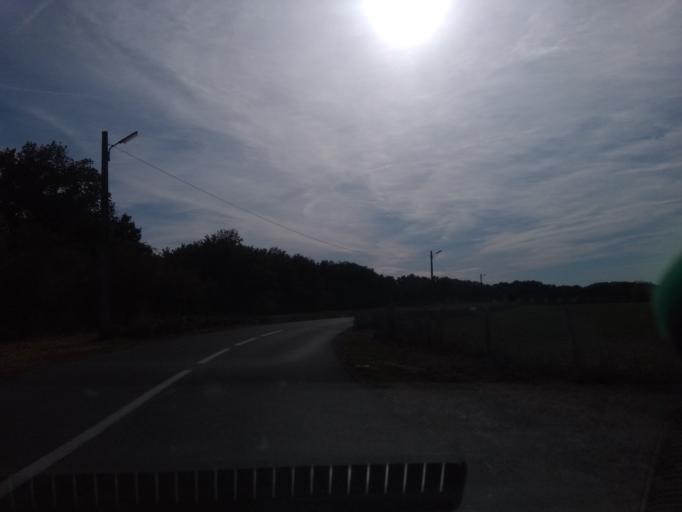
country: FR
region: Poitou-Charentes
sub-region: Departement de la Vienne
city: Saulge
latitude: 46.4051
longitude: 0.8913
